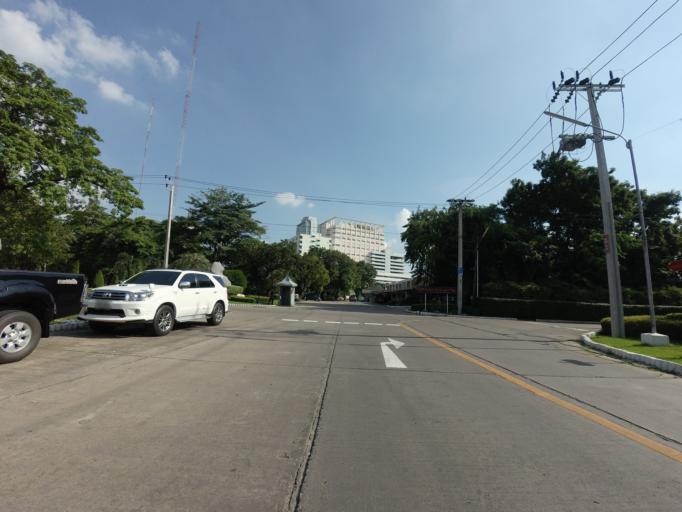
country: TH
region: Bangkok
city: Din Daeng
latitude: 13.7746
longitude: 100.5504
